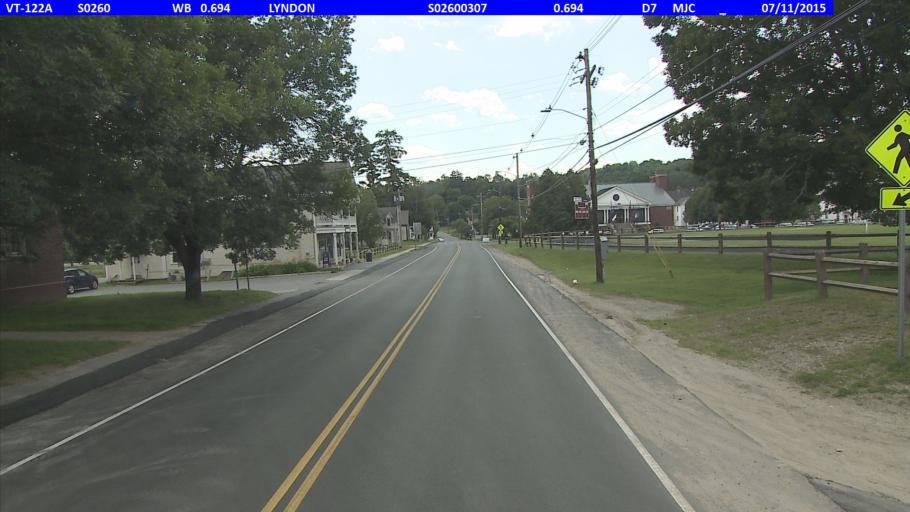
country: US
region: Vermont
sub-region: Caledonia County
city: Lyndonville
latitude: 44.5383
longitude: -72.0122
